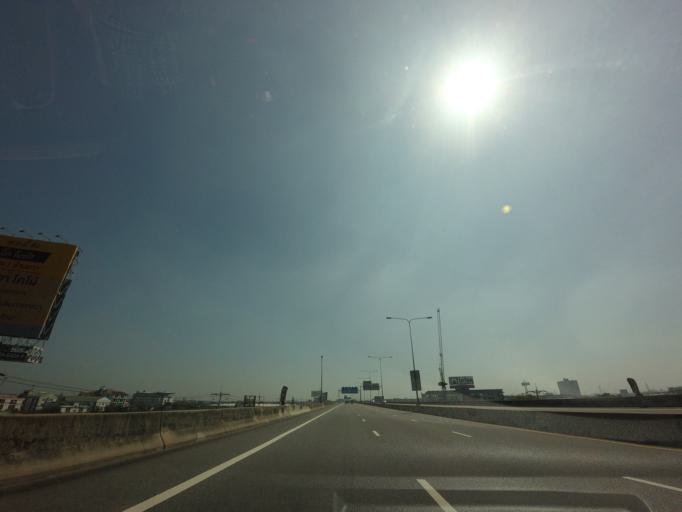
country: TH
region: Bangkok
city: Bang Na
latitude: 13.6544
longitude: 100.6739
